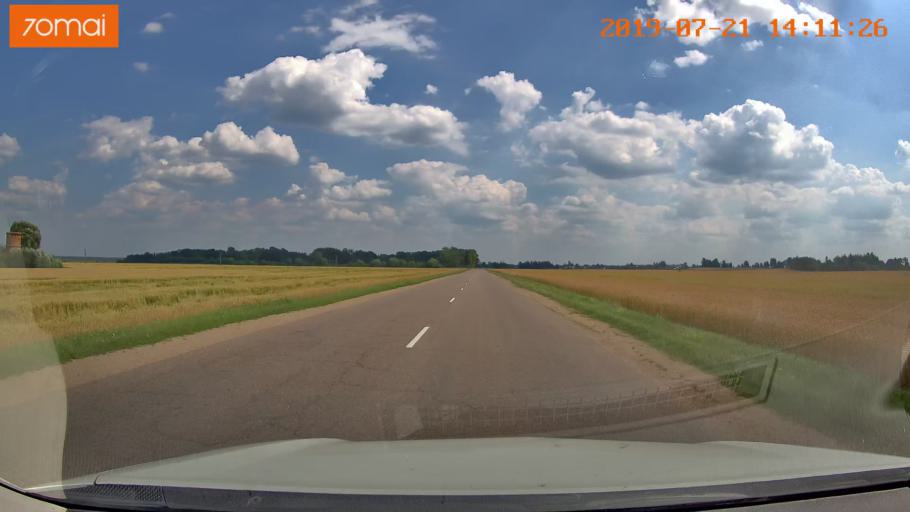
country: BY
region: Grodnenskaya
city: Karelichy
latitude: 53.6576
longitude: 26.1523
